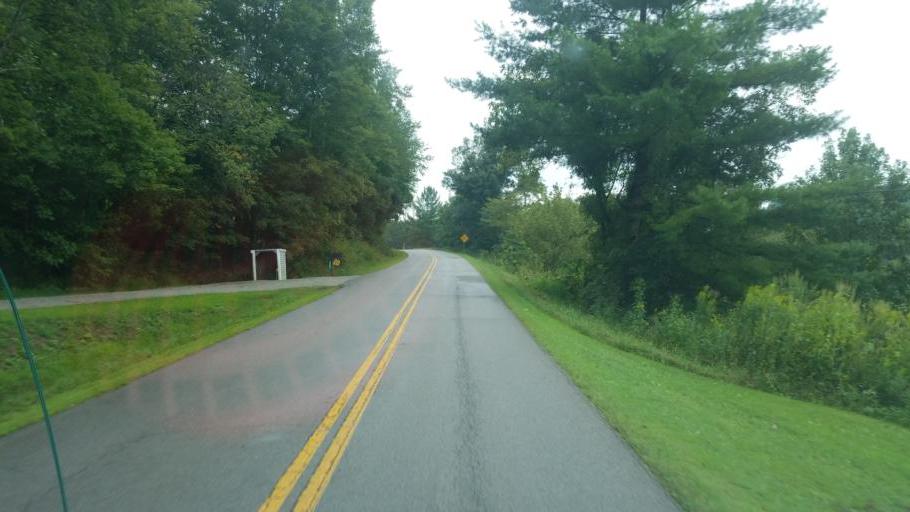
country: US
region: Kentucky
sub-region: Rowan County
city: Morehead
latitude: 38.3612
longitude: -83.5343
